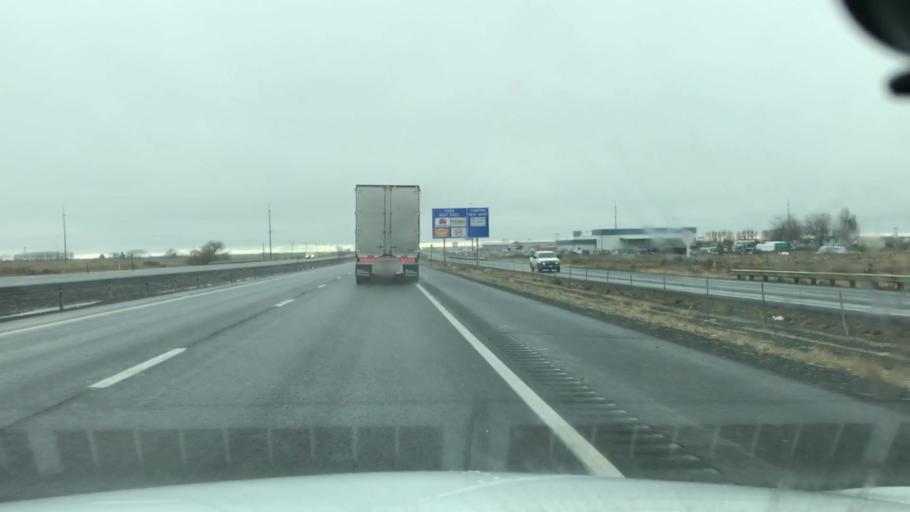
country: US
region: Washington
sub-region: Grant County
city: Moses Lake
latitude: 47.0947
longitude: -119.2084
